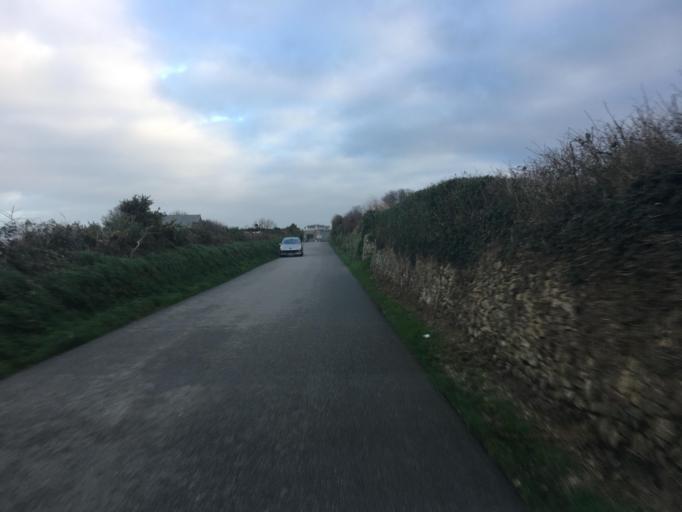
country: FR
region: Lower Normandy
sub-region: Departement de la Manche
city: Beaumont-Hague
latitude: 49.7114
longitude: -1.9258
